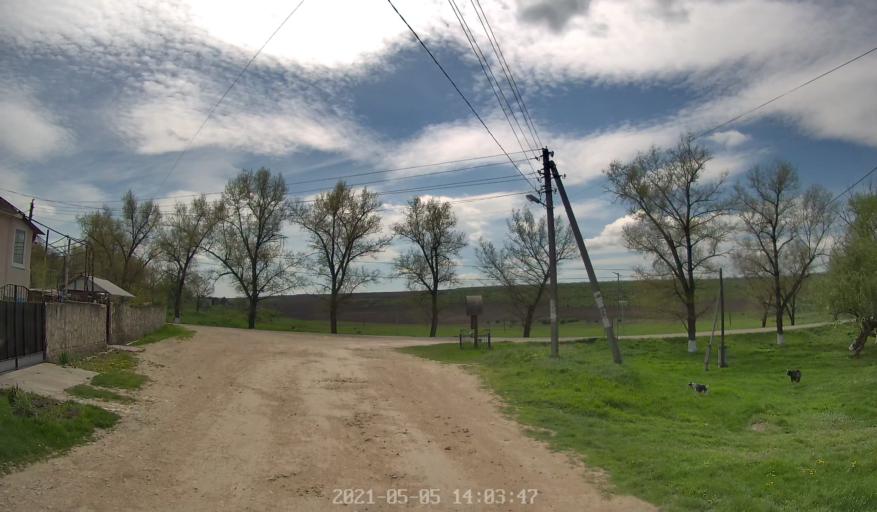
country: MD
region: Chisinau
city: Vadul lui Voda
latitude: 47.0628
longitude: 29.1337
